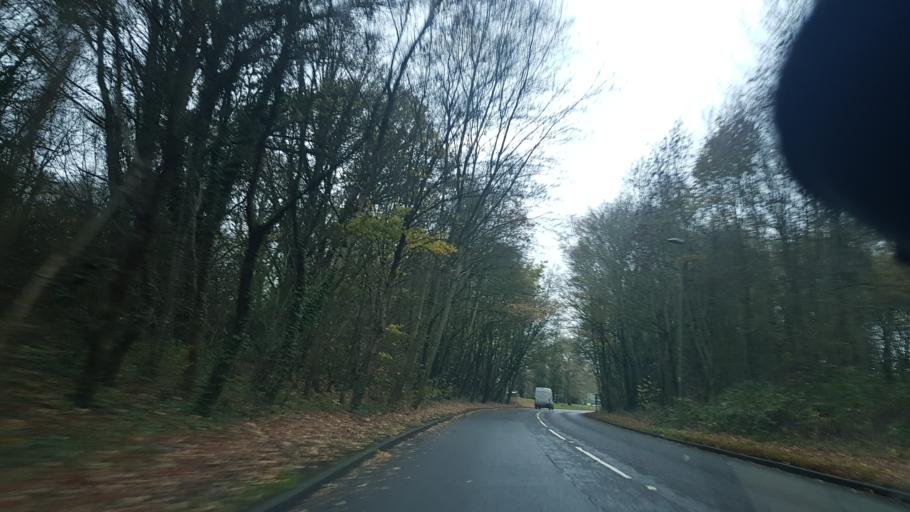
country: GB
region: England
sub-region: Surrey
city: Send
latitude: 51.2540
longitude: -0.5308
